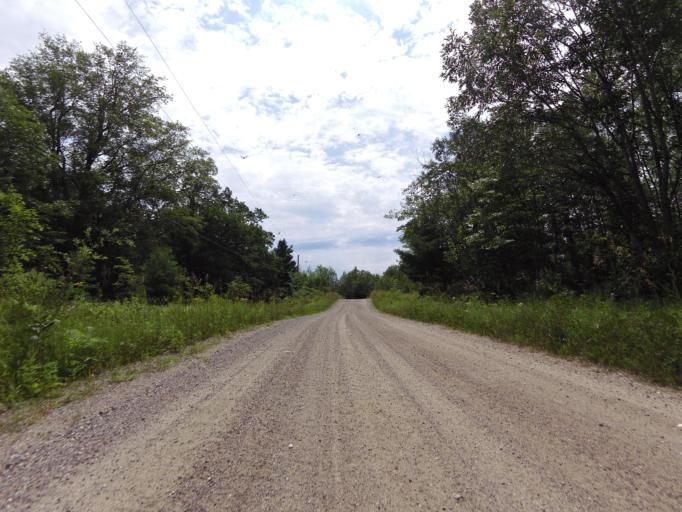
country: CA
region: Ontario
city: Perth
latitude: 44.7415
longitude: -76.6106
